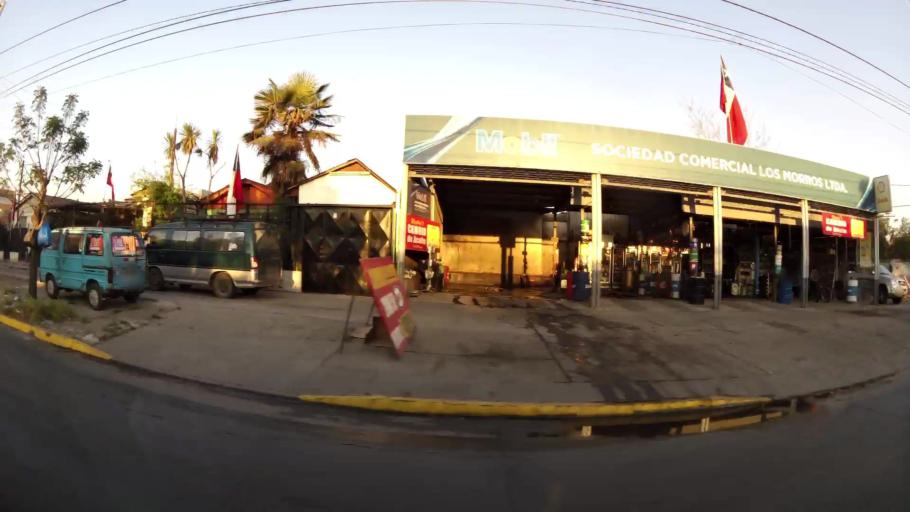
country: CL
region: Santiago Metropolitan
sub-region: Provincia de Maipo
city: San Bernardo
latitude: -33.5674
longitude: -70.6724
